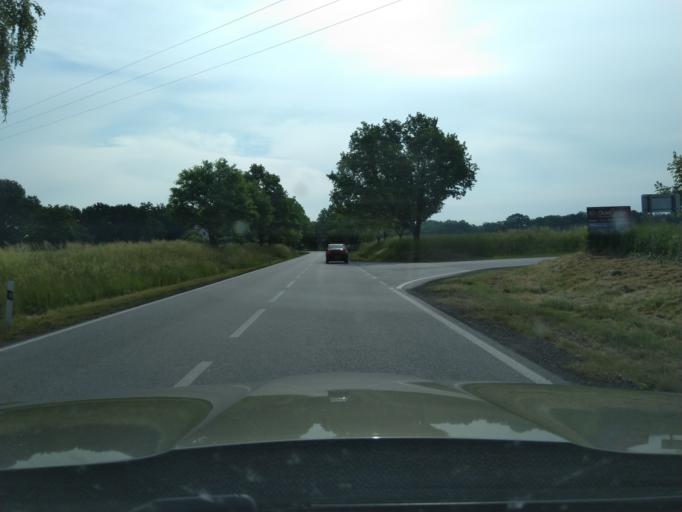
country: CZ
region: Jihocesky
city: Zliv
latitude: 49.0304
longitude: 14.3321
